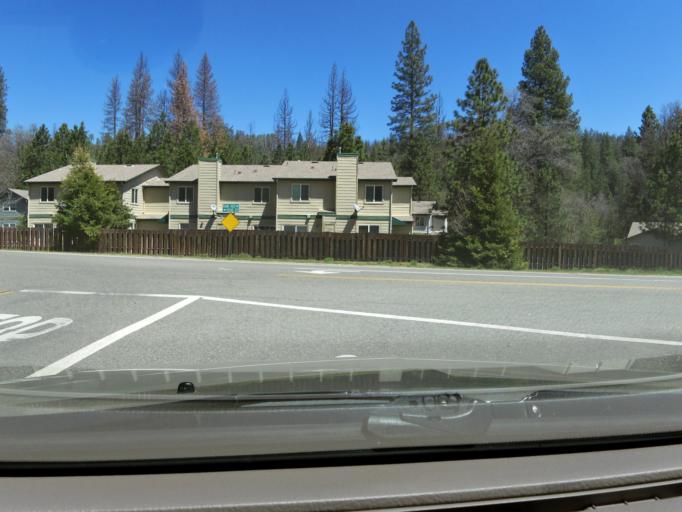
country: US
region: California
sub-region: Madera County
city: Oakhurst
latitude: 37.3354
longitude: -119.5819
